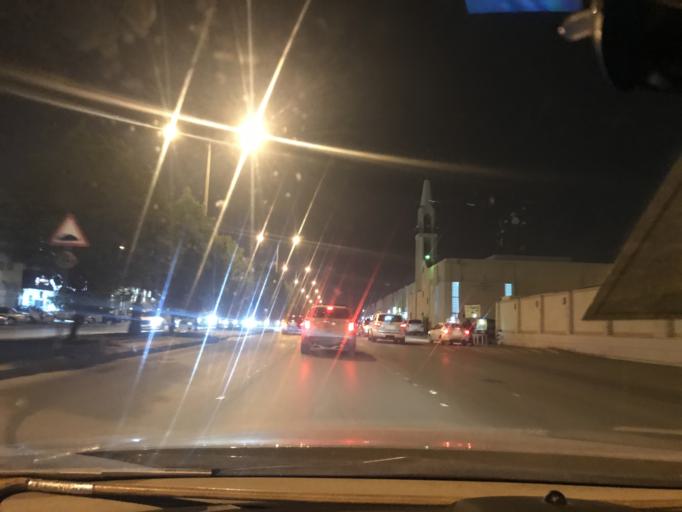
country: SA
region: Ar Riyad
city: Riyadh
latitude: 24.7567
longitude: 46.7520
